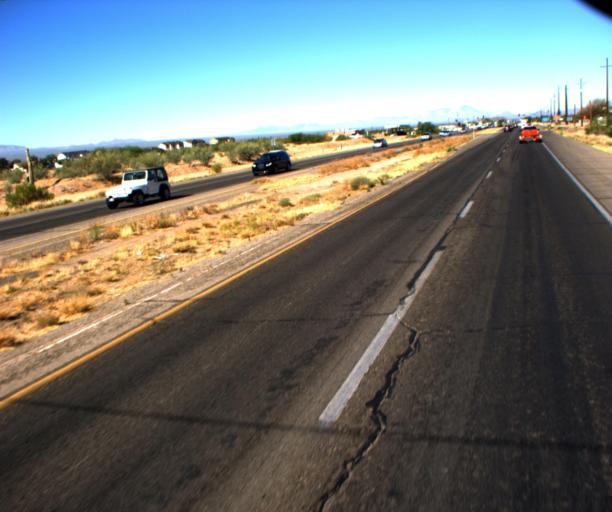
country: US
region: Arizona
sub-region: Pima County
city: Tucson Estates
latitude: 32.1724
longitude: -111.0678
